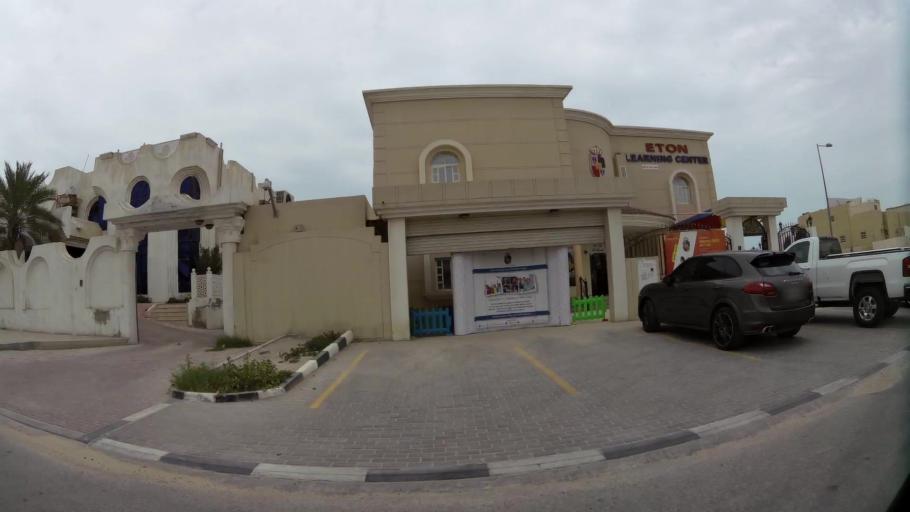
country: QA
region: Baladiyat ar Rayyan
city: Ar Rayyan
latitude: 25.3406
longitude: 51.4649
